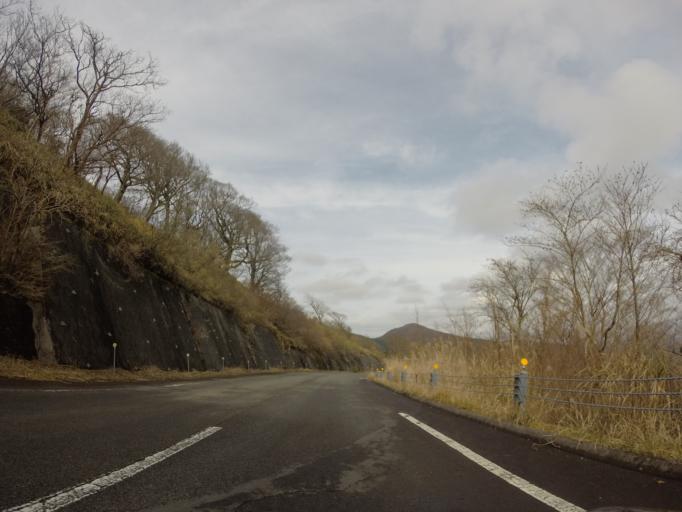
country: JP
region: Shizuoka
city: Heda
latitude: 34.8675
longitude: 138.8403
